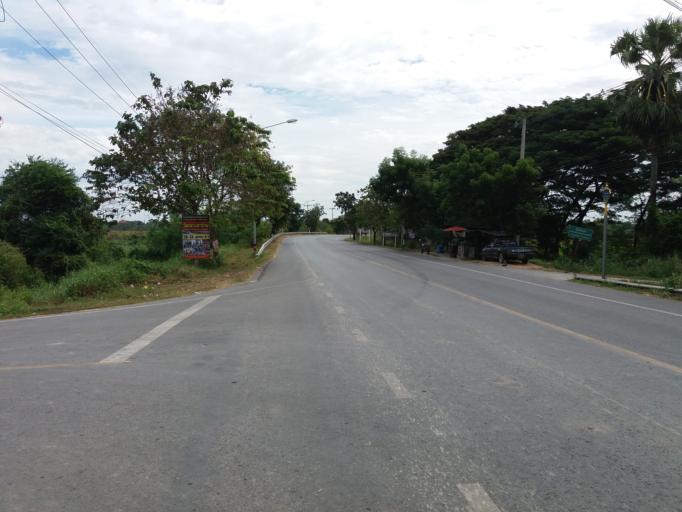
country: TH
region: Sing Buri
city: Bang Racham
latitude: 14.8831
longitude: 100.3503
